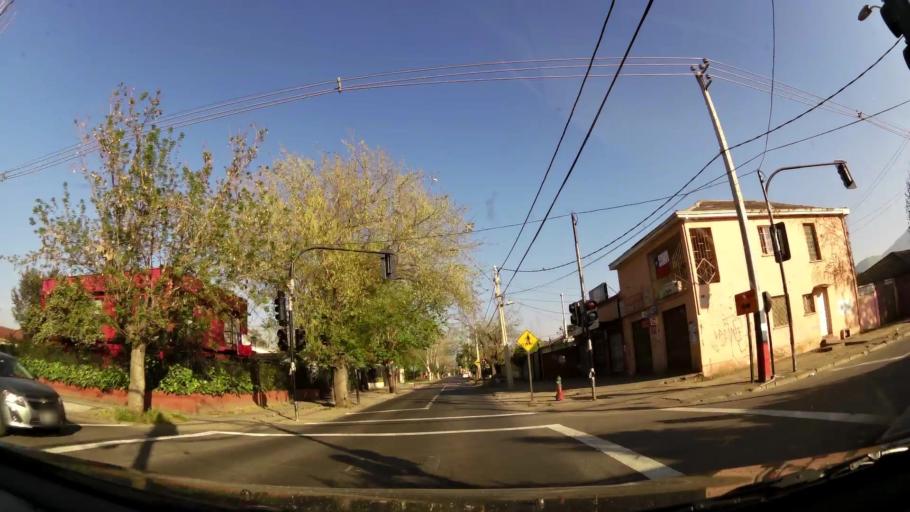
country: CL
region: Santiago Metropolitan
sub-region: Provincia de Santiago
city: Santiago
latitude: -33.3924
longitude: -70.6356
